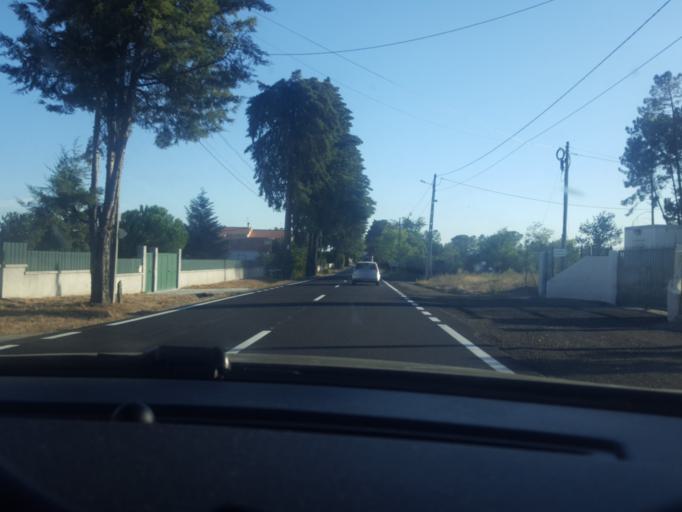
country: PT
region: Viseu
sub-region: Mangualde
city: Mangualde
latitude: 40.5829
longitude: -7.8056
